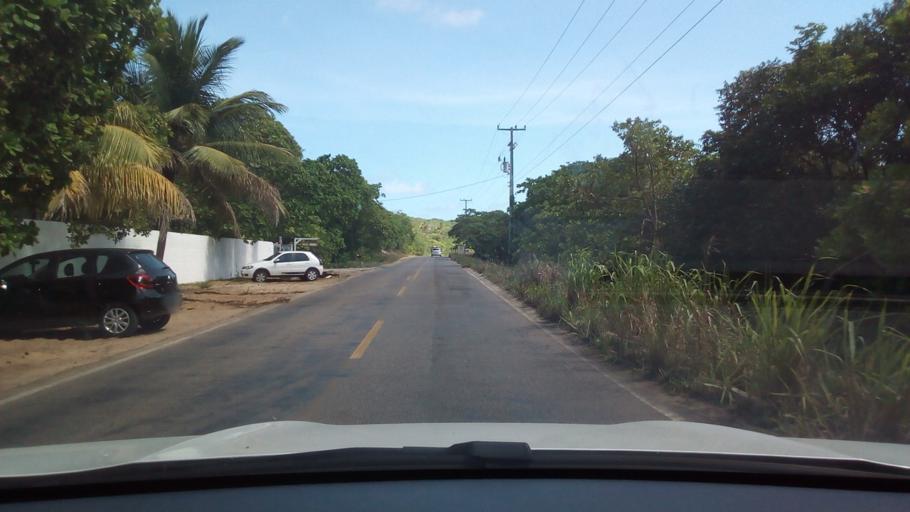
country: BR
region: Rio Grande do Norte
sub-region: Ares
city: Ares
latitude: -6.2242
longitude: -35.0704
